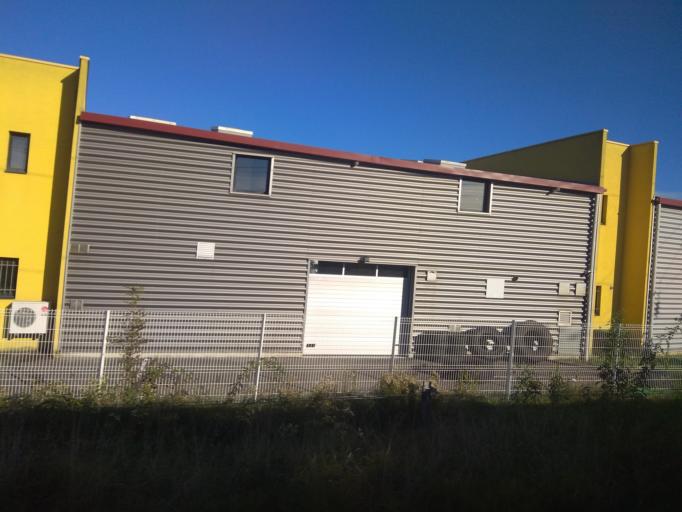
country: FR
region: Rhone-Alpes
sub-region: Departement de la Haute-Savoie
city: Pringy
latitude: 45.9403
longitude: 6.1234
